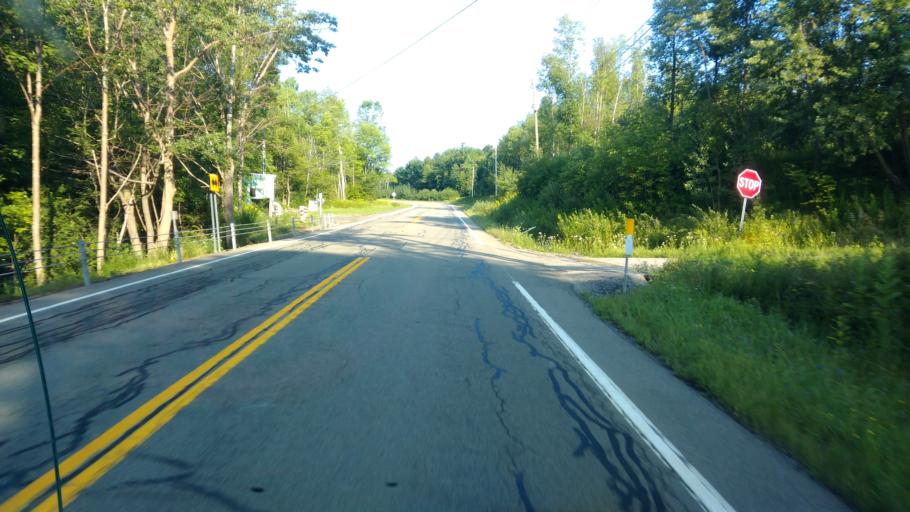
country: US
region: New York
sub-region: Allegany County
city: Andover
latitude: 42.1532
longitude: -77.6972
